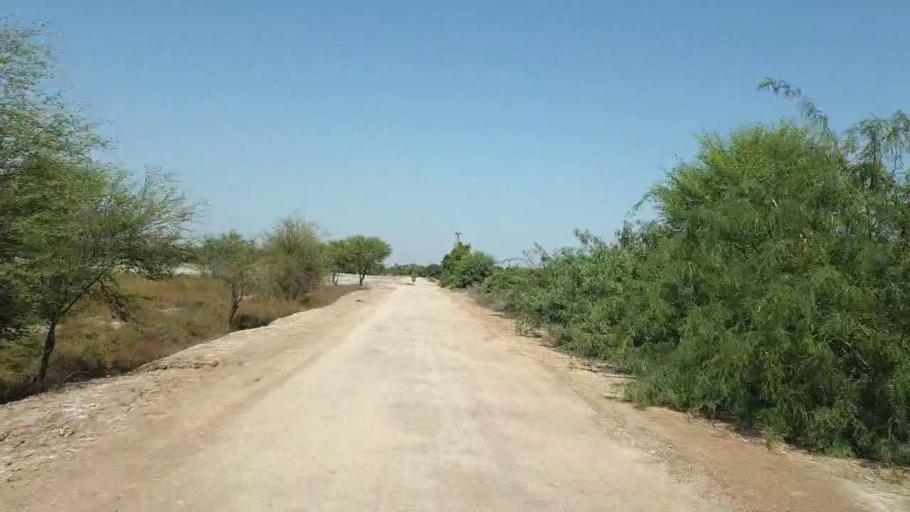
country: PK
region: Sindh
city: Tando Jam
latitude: 25.4186
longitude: 68.4574
